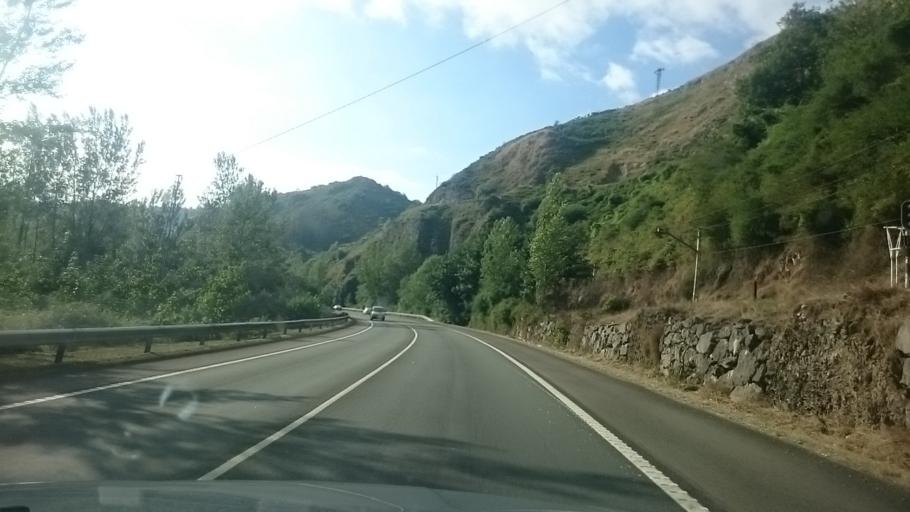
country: ES
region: Asturias
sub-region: Province of Asturias
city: Sama
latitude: 43.3305
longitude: -5.7493
